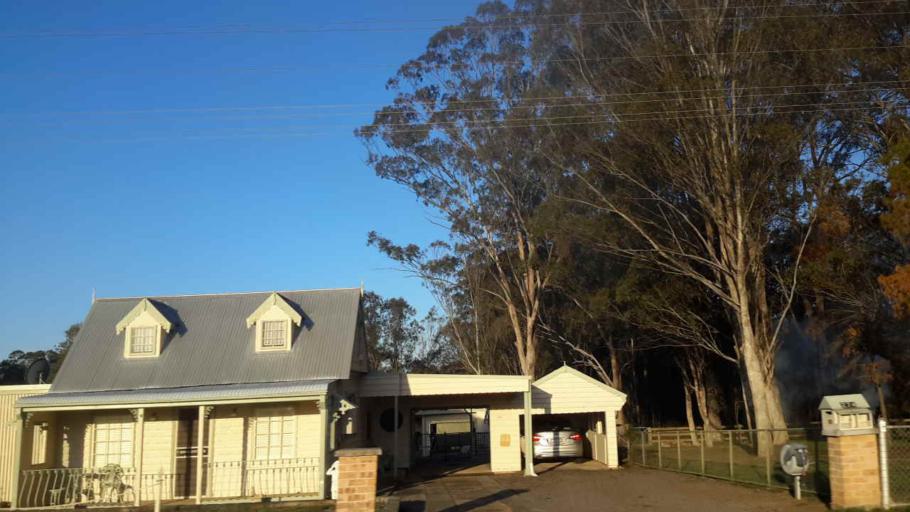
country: AU
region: New South Wales
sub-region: Wollondilly
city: Douglas Park
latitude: -34.2134
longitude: 150.7216
